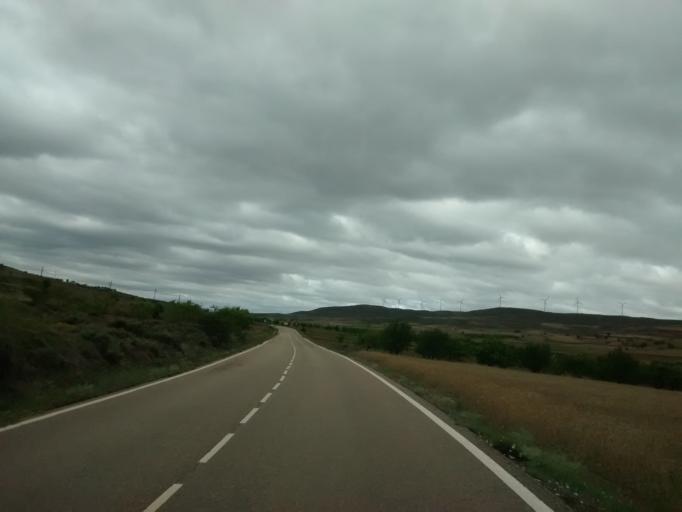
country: ES
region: Aragon
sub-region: Provincia de Zaragoza
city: Trasmoz
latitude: 41.8422
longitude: -1.7182
